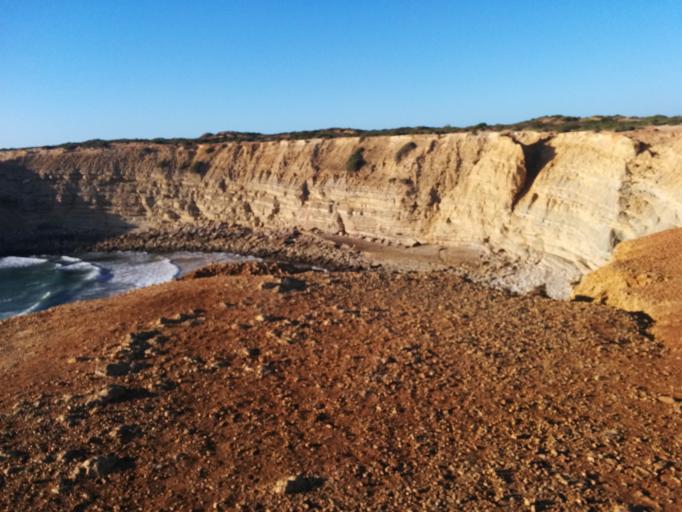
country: PT
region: Faro
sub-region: Vila do Bispo
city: Vila do Bispo
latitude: 37.1881
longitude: -8.9096
